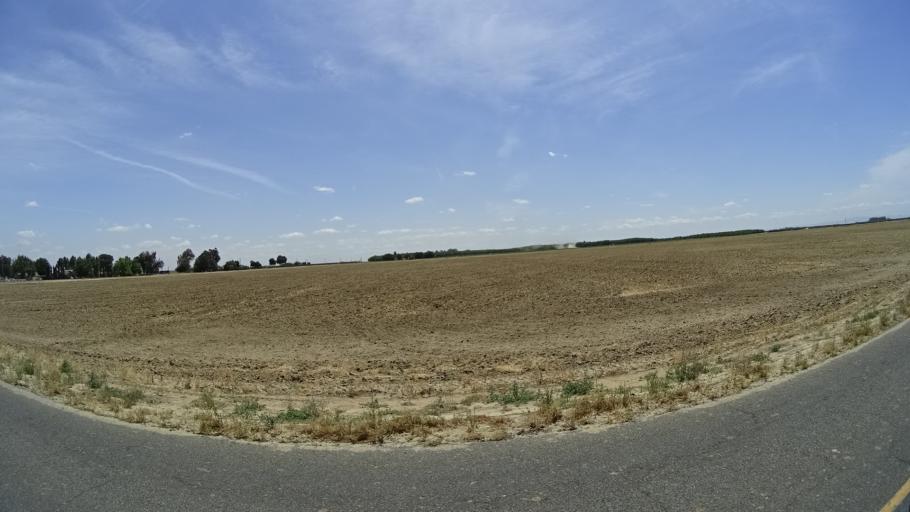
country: US
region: California
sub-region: Kings County
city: Home Garden
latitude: 36.2838
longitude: -119.6748
